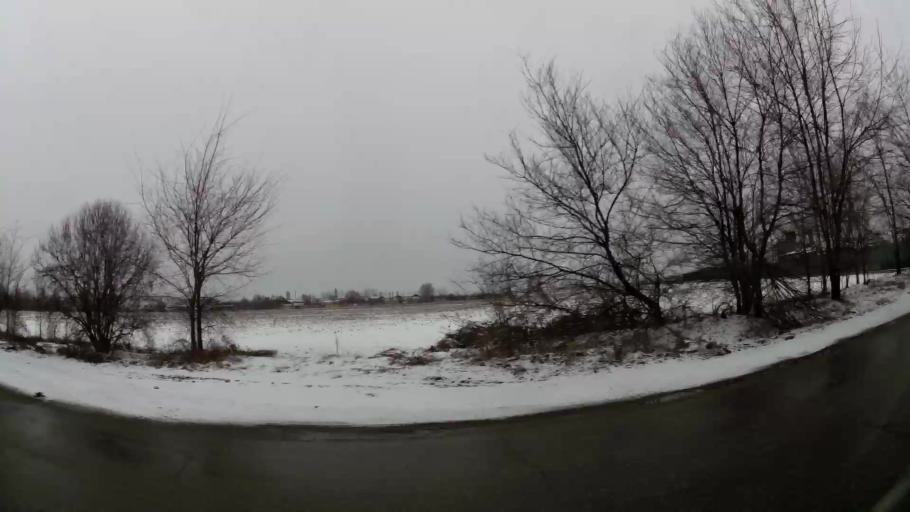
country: RO
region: Dambovita
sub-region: Comuna Ulmi
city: Ulmi
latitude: 44.8961
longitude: 25.5090
